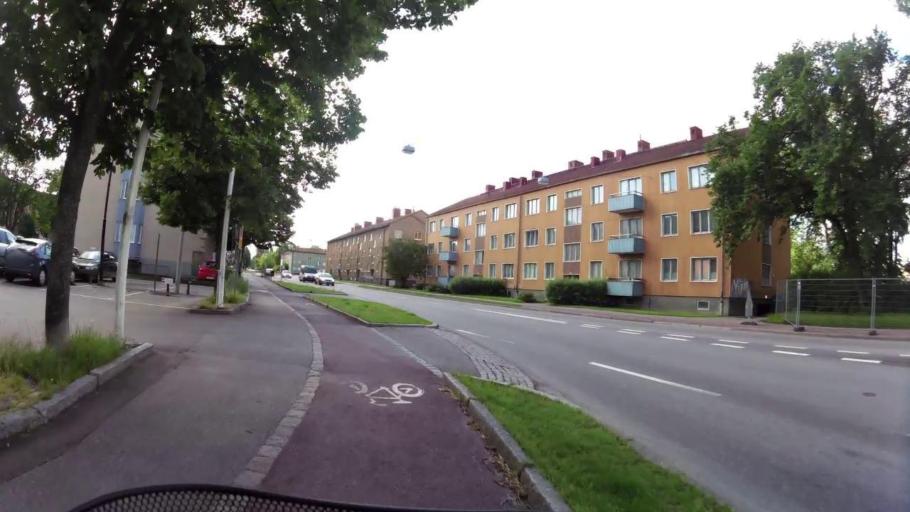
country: SE
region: OEstergoetland
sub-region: Linkopings Kommun
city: Linkoping
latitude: 58.4117
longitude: 15.6343
